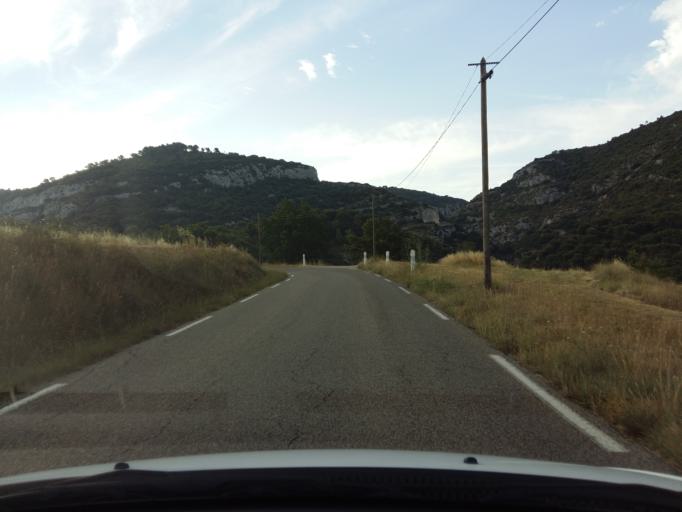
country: FR
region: Provence-Alpes-Cote d'Azur
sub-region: Departement du Vaucluse
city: Venasque
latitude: 43.9850
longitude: 5.1749
